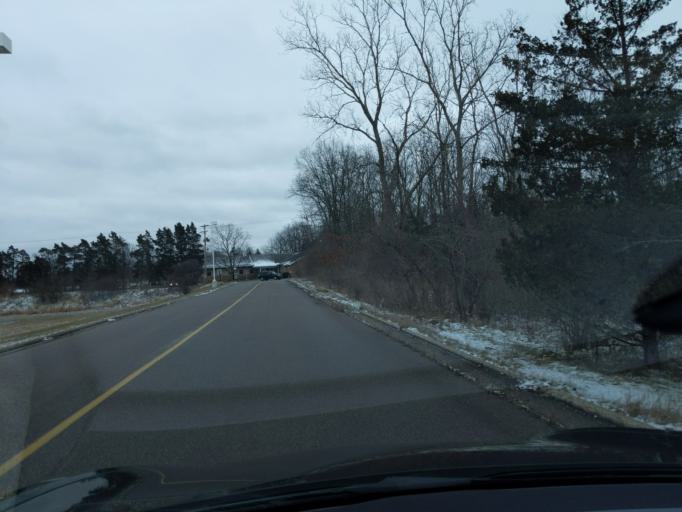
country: US
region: Michigan
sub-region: Ingham County
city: Okemos
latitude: 42.7178
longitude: -84.4261
